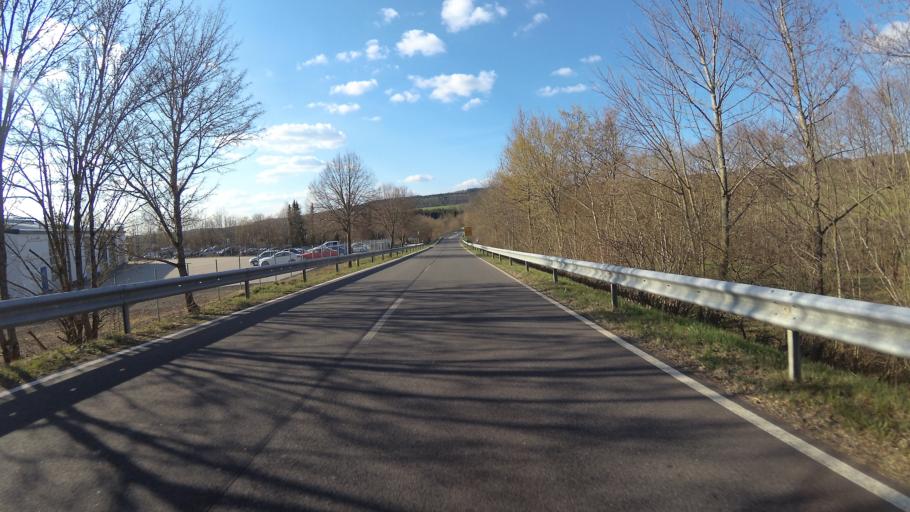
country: DE
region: Rheinland-Pfalz
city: Mullenbach
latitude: 50.3185
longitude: 6.9216
